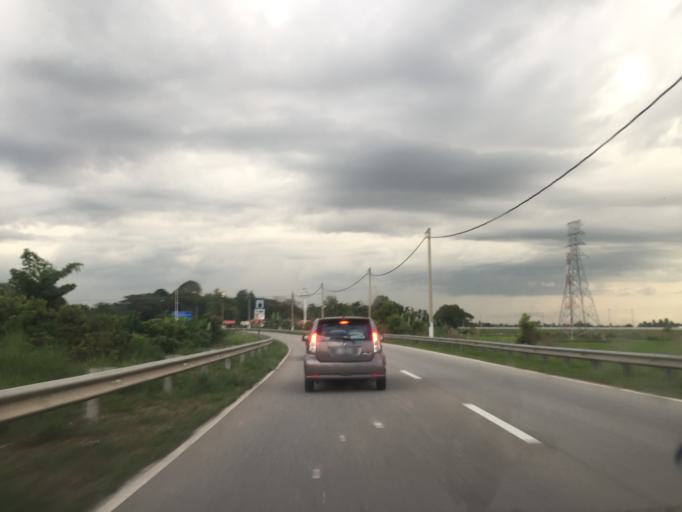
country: MY
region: Penang
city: Tasek Glugor
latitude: 5.5574
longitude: 100.5004
